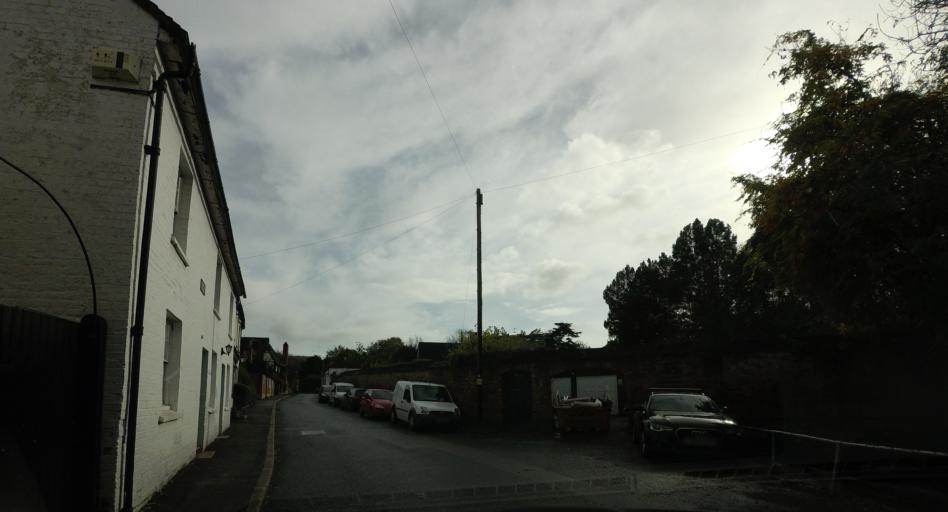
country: GB
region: England
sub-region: Kent
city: Shoreham
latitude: 51.3332
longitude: 0.1819
